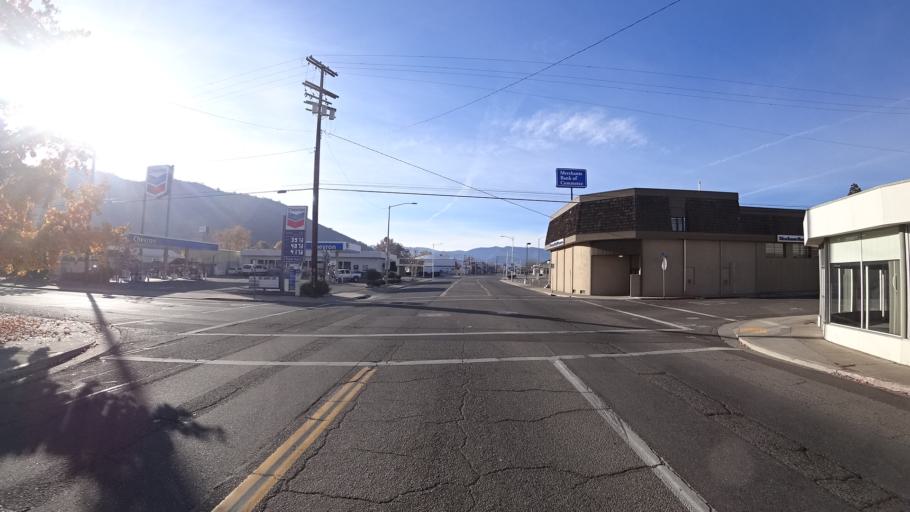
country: US
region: California
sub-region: Siskiyou County
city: Yreka
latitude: 41.7310
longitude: -122.6358
